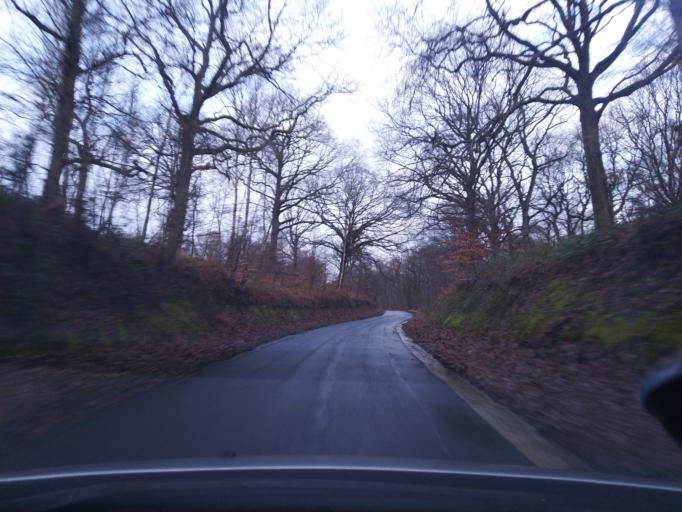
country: FR
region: Haute-Normandie
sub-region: Departement de la Seine-Maritime
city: Saint-Pierre-de-Varengeville
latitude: 49.4916
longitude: 0.9049
